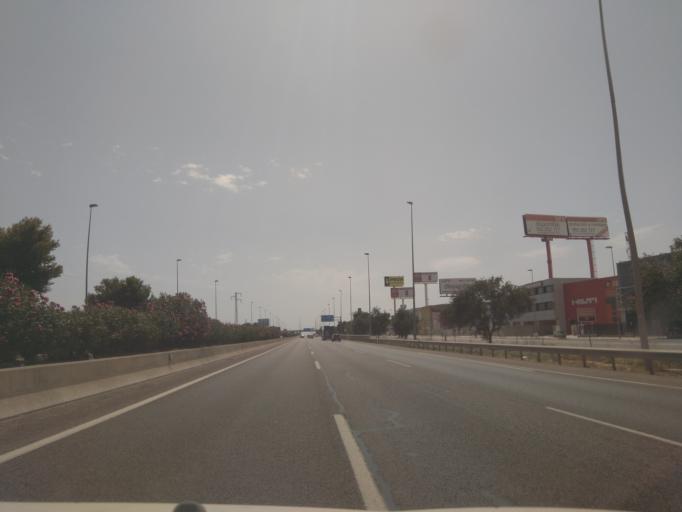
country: ES
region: Valencia
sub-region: Provincia de Valencia
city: Alfafar
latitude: 39.4062
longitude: -0.3832
